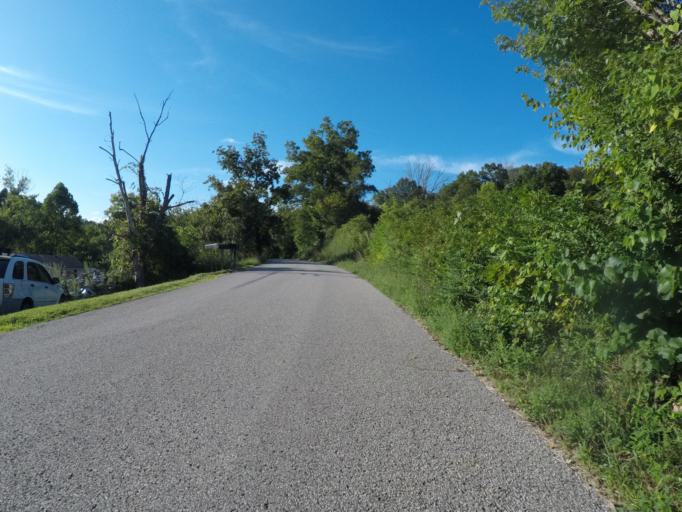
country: US
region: West Virginia
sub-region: Cabell County
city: Huntington
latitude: 38.5182
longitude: -82.5010
